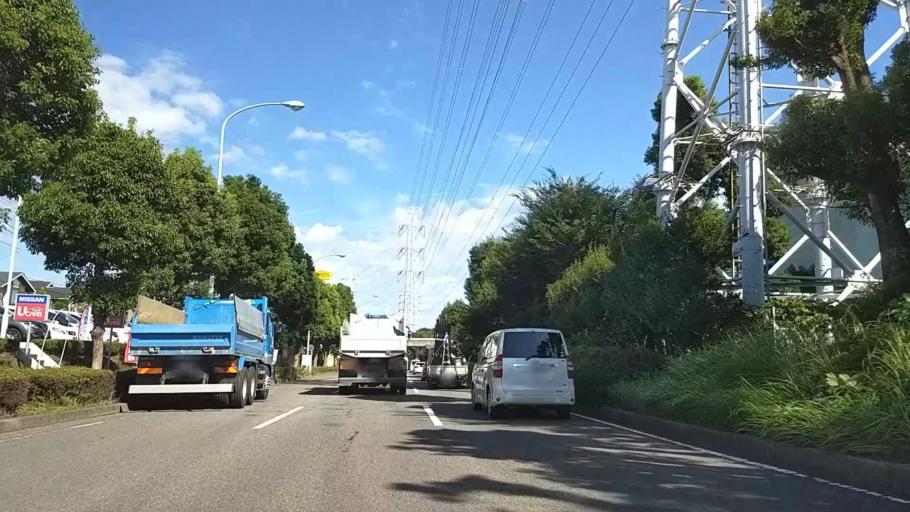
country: JP
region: Tokyo
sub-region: Machida-shi
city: Machida
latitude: 35.5405
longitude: 139.5624
